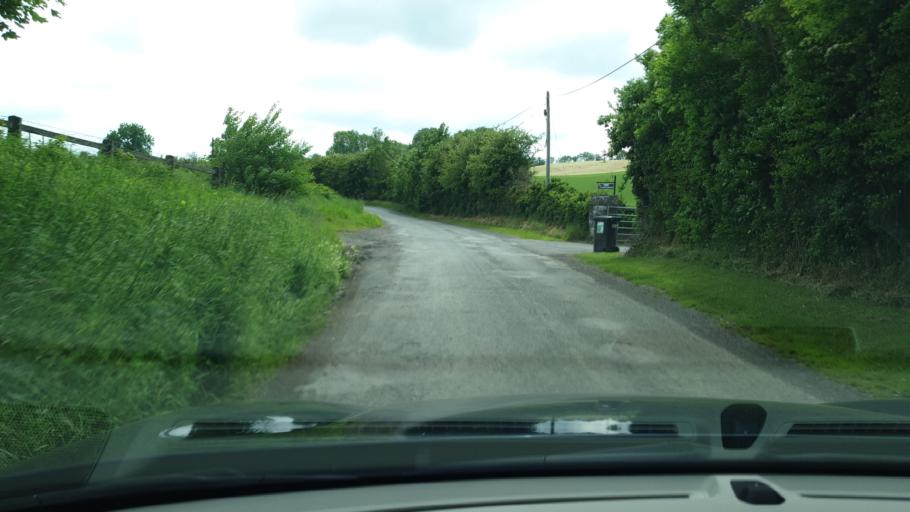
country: IE
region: Ulster
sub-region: An Cabhan
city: Kingscourt
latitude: 53.7989
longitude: -6.7222
